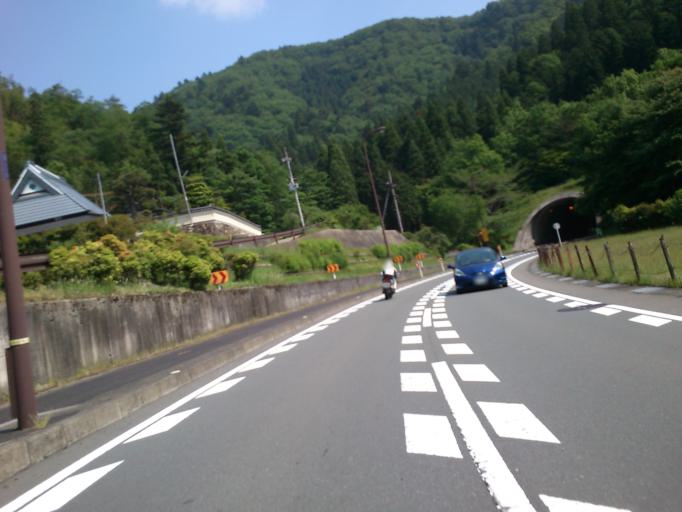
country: JP
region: Kyoto
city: Kameoka
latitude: 35.2310
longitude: 135.5738
